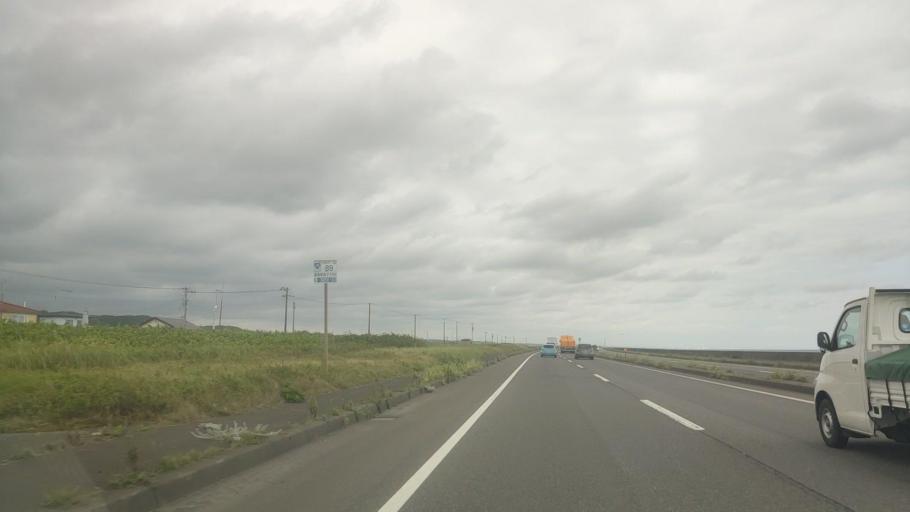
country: JP
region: Hokkaido
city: Shiraoi
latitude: 42.5526
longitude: 141.3696
